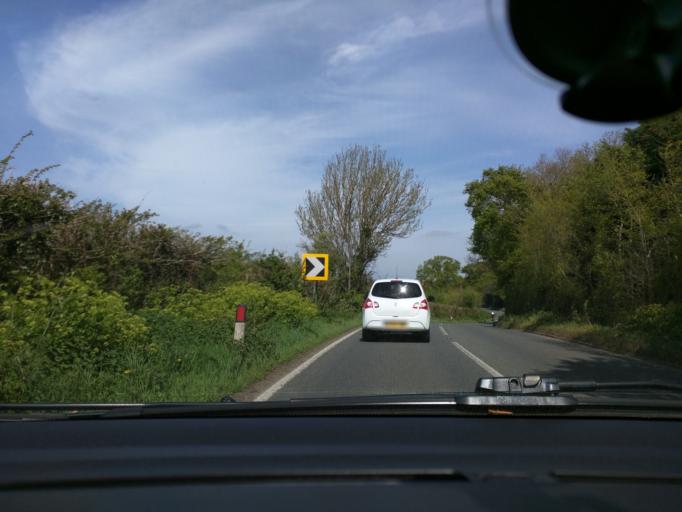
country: GB
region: England
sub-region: Suffolk
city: Leiston
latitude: 52.2302
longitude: 1.5749
